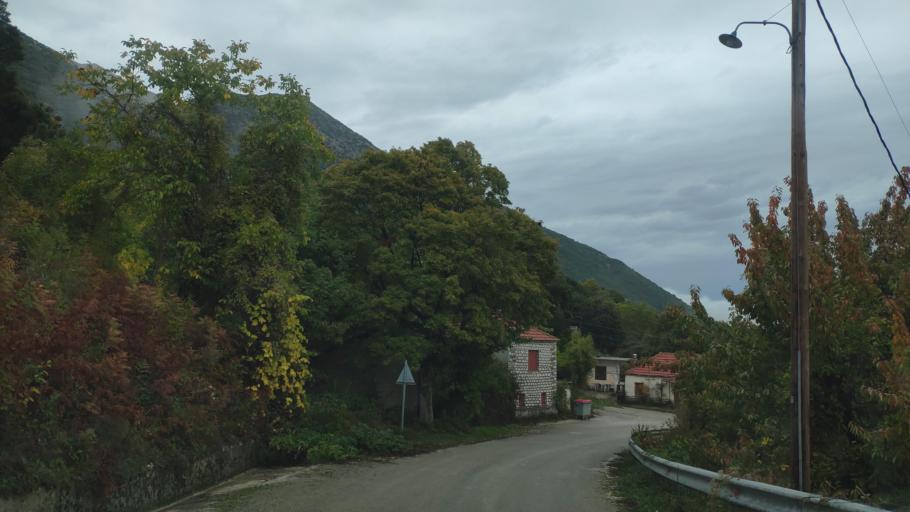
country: GR
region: Epirus
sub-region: Nomos Thesprotias
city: Paramythia
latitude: 39.4591
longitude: 20.6696
